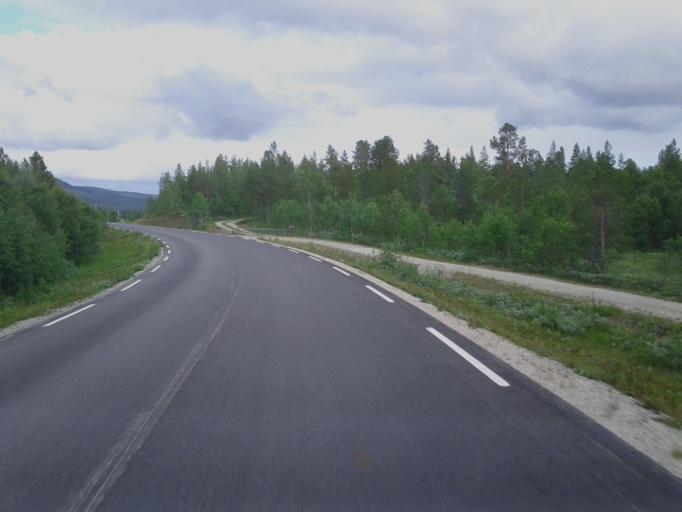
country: NO
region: Sor-Trondelag
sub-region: Roros
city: Roros
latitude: 62.3079
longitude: 11.6870
